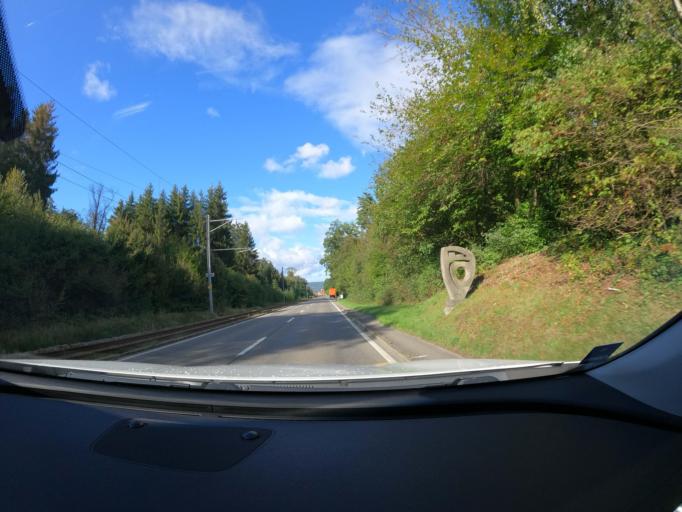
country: CH
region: Aargau
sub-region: Bezirk Lenzburg
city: Staufen
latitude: 47.3657
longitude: 8.1657
